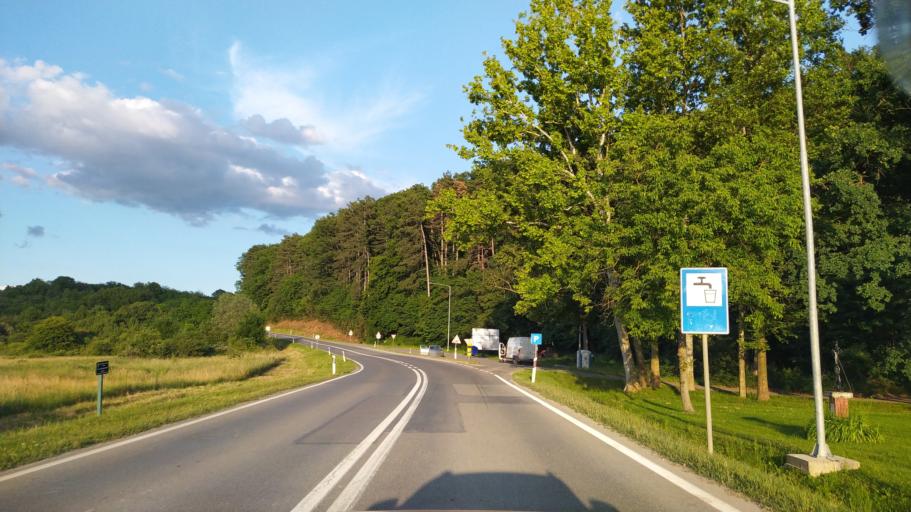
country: HR
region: Osjecko-Baranjska
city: Martin
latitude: 45.4906
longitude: 18.0284
